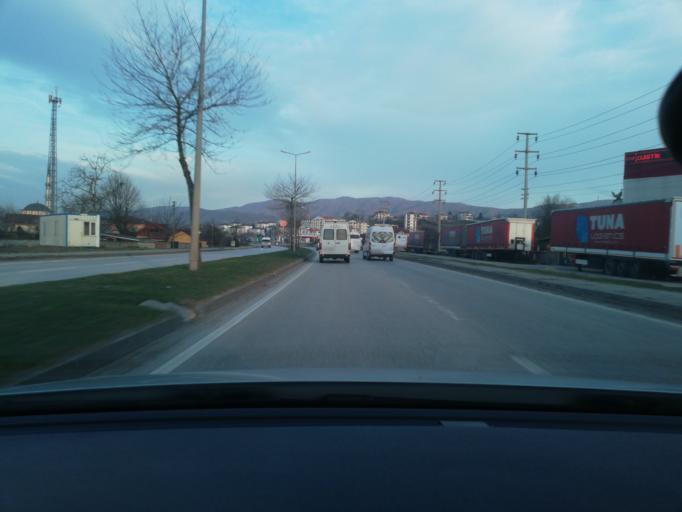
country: TR
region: Duzce
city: Konuralp
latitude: 40.8982
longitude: 31.1629
